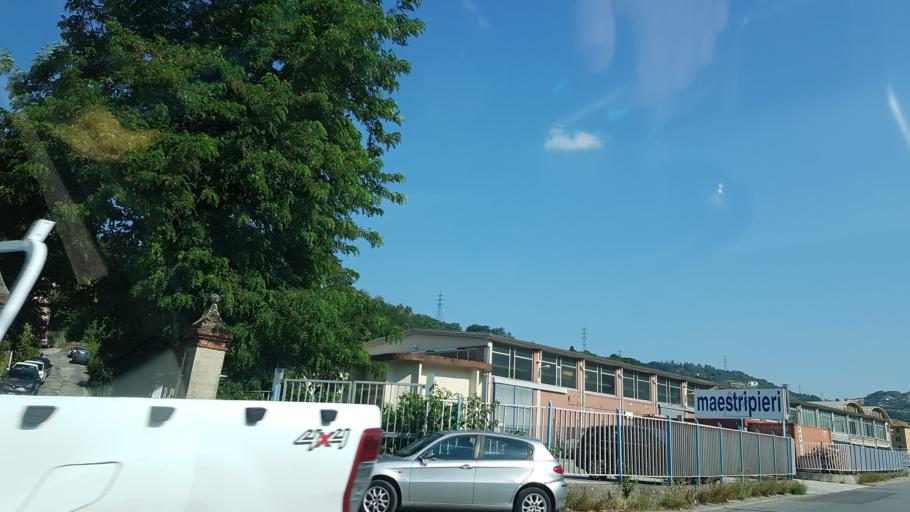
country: IT
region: Liguria
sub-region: Provincia di Genova
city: Manesseno
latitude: 44.4869
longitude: 8.9214
